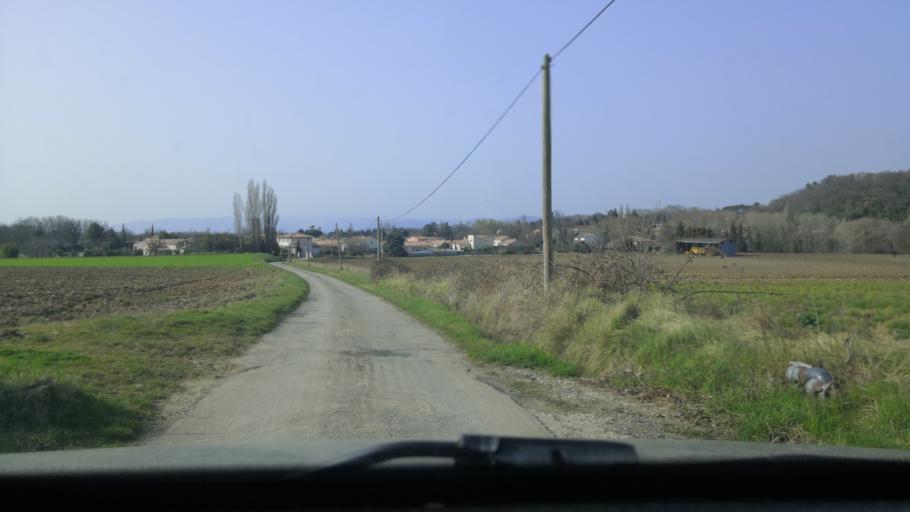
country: FR
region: Rhone-Alpes
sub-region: Departement de la Drome
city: La Begude-de-Mazenc
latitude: 44.5399
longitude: 4.9410
